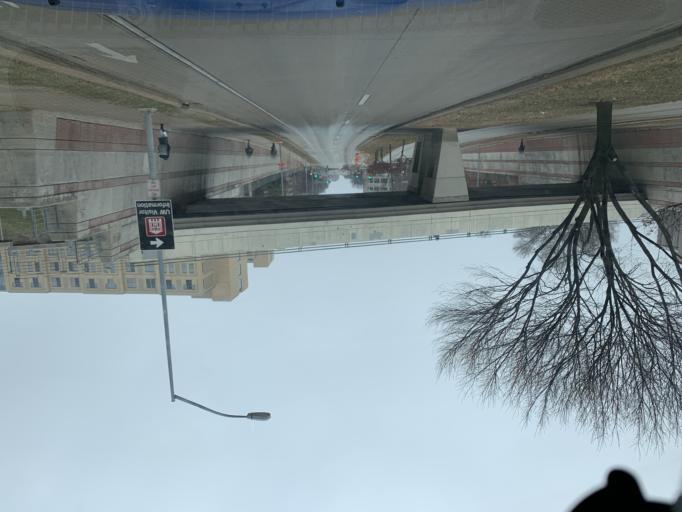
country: US
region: Wisconsin
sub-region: Dane County
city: Madison
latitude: 43.0695
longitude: -89.4009
